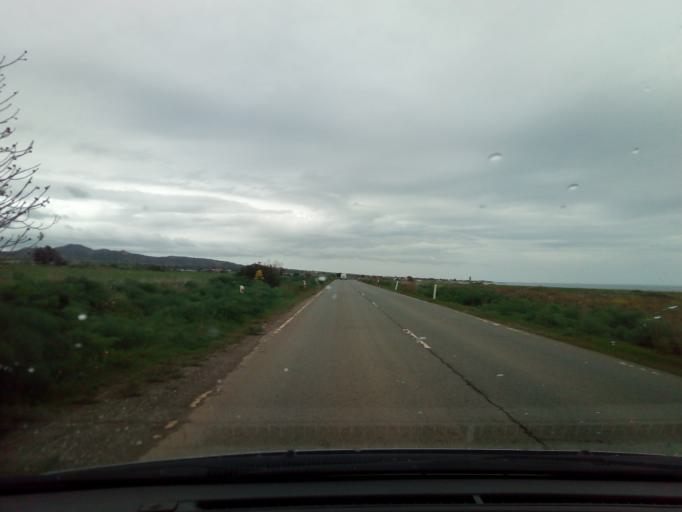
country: CY
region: Larnaka
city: Kofinou
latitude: 34.7416
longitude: 33.3808
